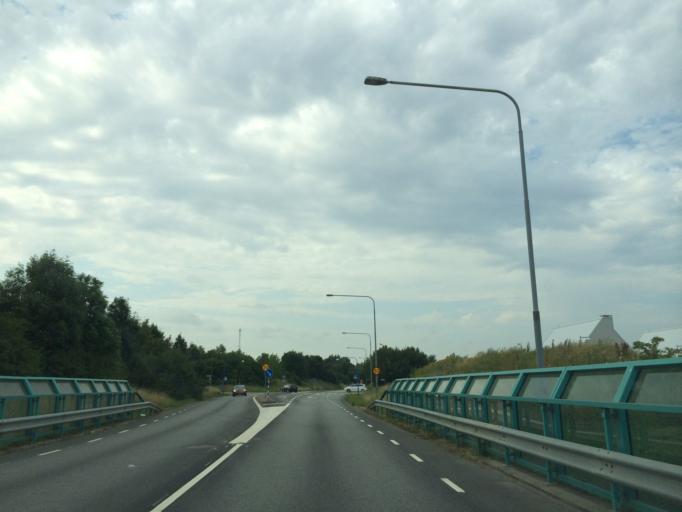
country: SE
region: Skane
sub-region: Burlovs Kommun
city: Arloev
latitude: 55.5900
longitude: 13.1047
